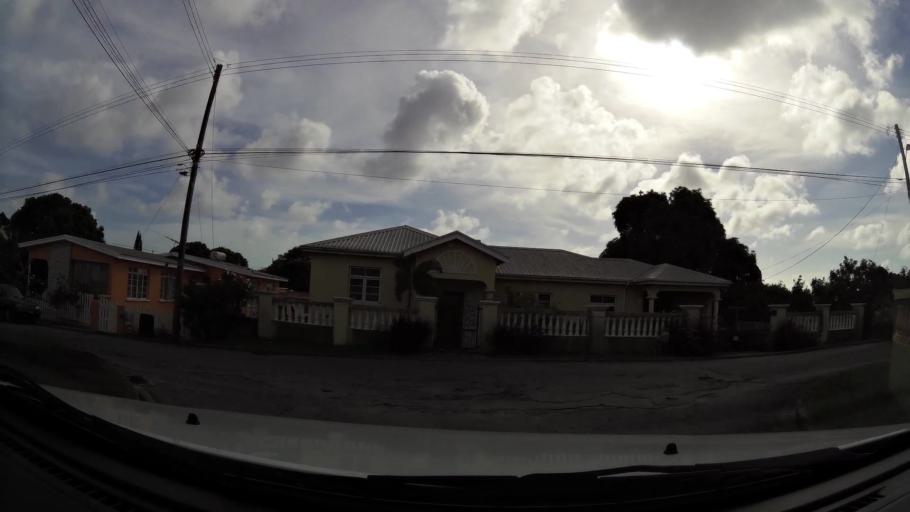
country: BB
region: Saint Michael
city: Bridgetown
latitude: 13.0836
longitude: -59.5819
